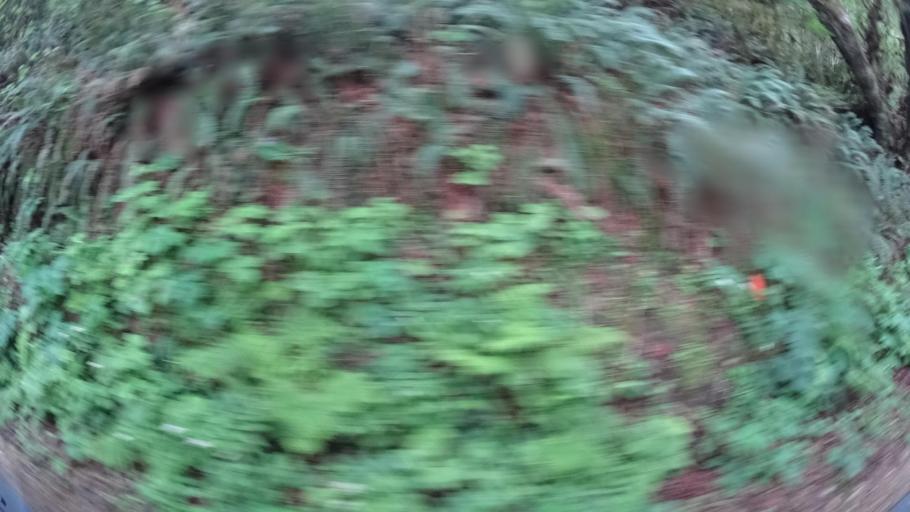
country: US
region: California
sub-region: Humboldt County
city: Ferndale
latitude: 40.5387
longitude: -124.2771
